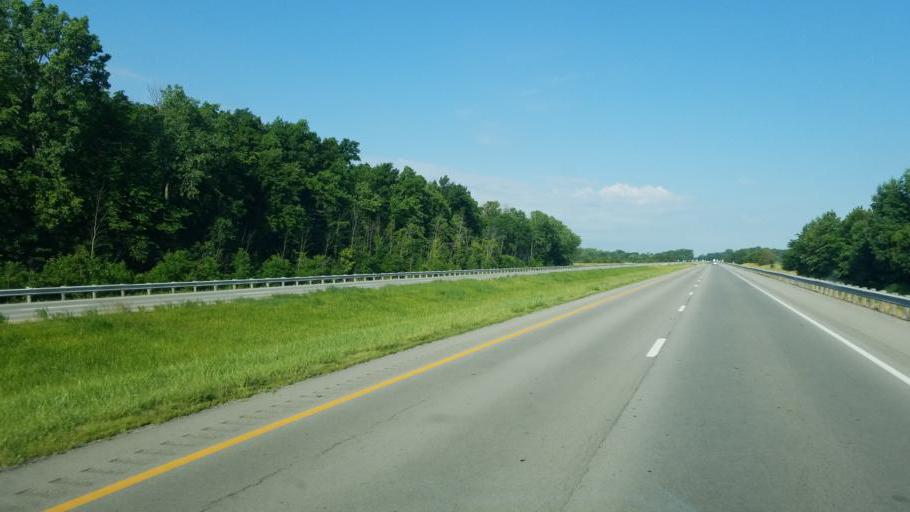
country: US
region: Ohio
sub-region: Hancock County
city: Findlay
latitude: 40.9820
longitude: -83.5243
